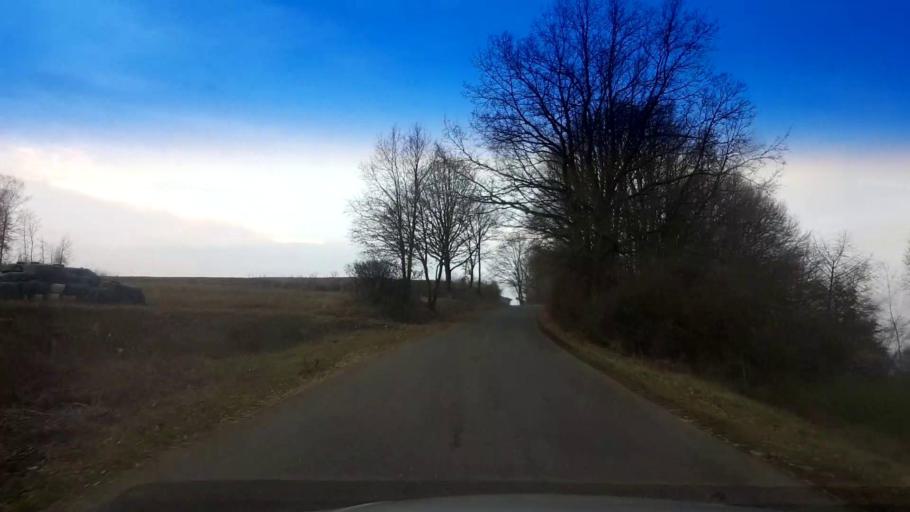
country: DE
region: Bavaria
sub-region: Upper Franconia
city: Hirschaid
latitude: 49.8013
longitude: 10.9909
